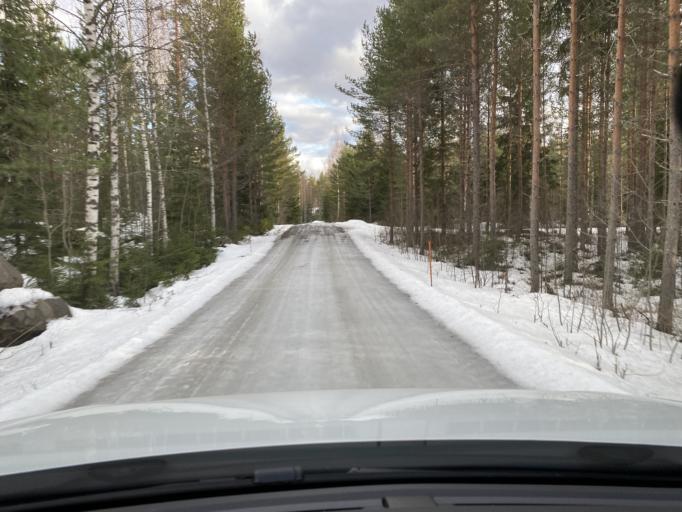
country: FI
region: Pirkanmaa
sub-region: Lounais-Pirkanmaa
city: Mouhijaervi
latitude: 61.4335
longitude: 22.9865
